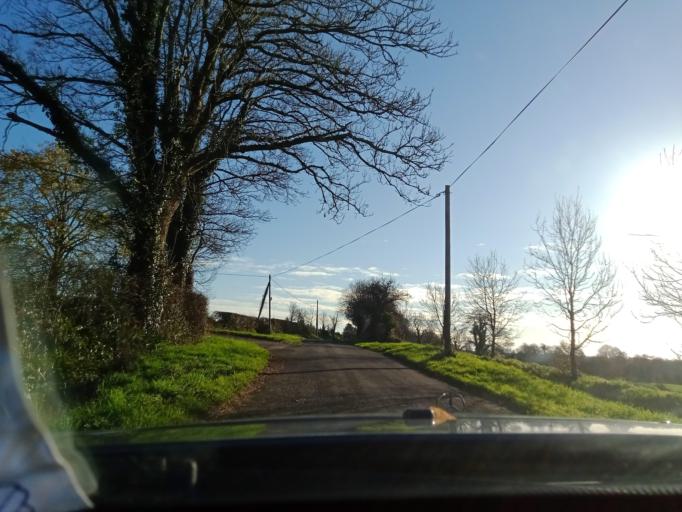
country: IE
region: Leinster
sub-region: Kilkenny
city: Mooncoin
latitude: 52.3378
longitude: -7.2654
